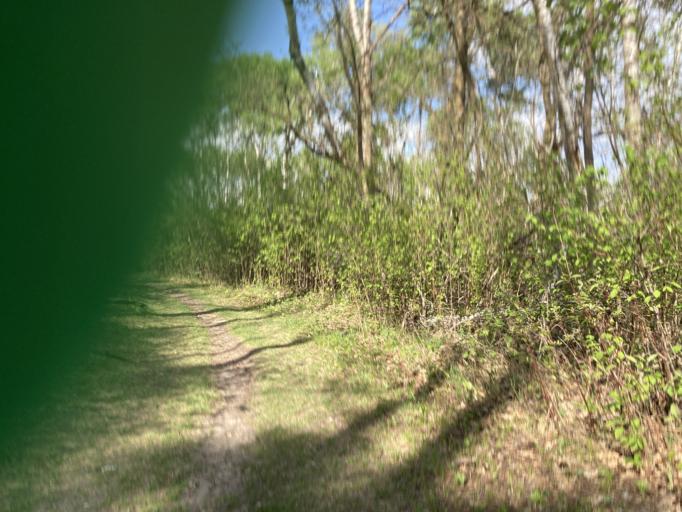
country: CA
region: Manitoba
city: Brandon
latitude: 49.7201
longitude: -99.8969
